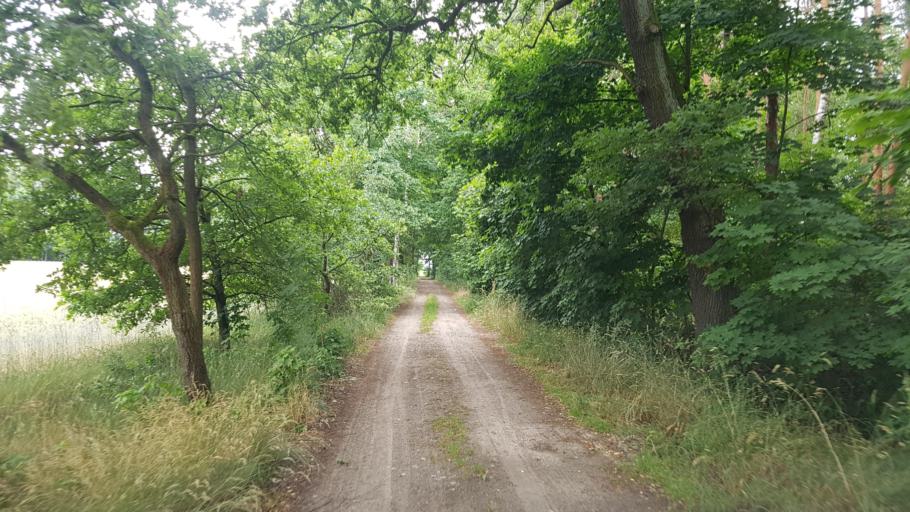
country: DE
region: Brandenburg
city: Schraden
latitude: 51.4207
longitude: 13.6850
